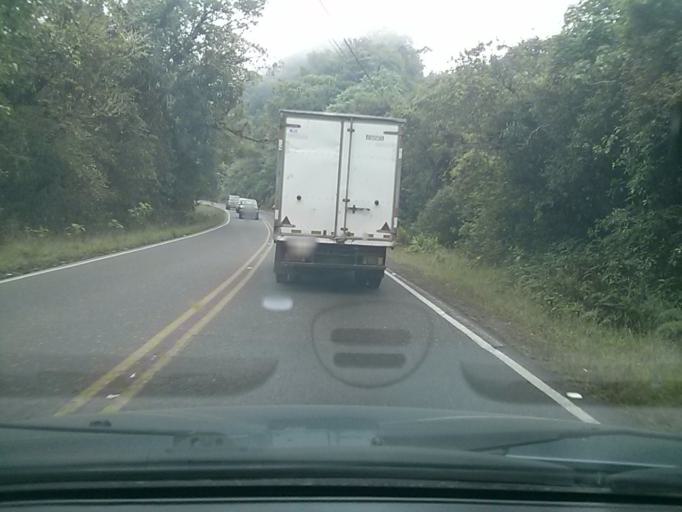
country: CR
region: San Jose
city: San Marcos
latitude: 9.7384
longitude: -83.9560
